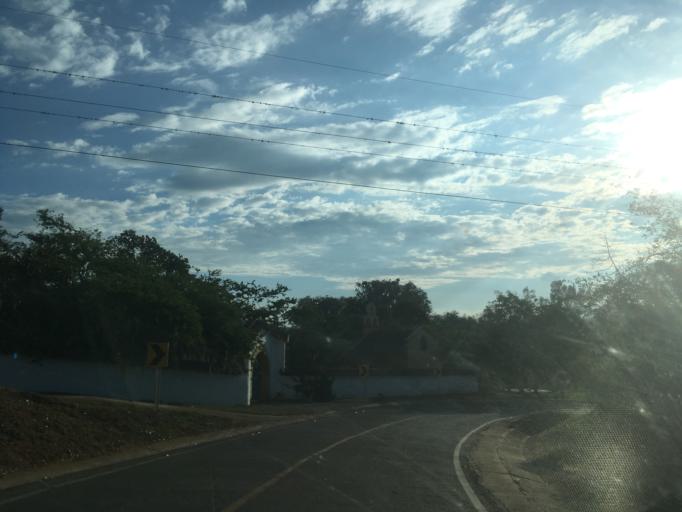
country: CO
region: Santander
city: Barichara
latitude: 6.6359
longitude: -73.2005
